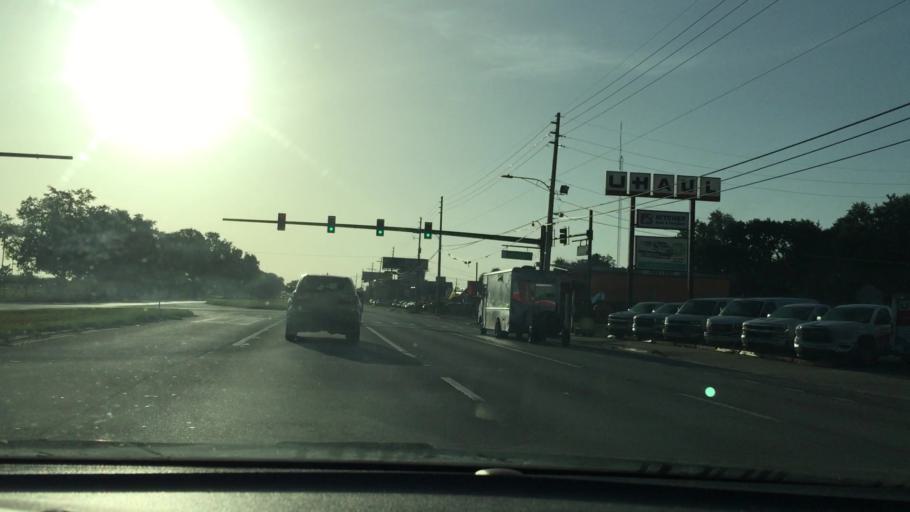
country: US
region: Florida
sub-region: Orange County
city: Pine Hills
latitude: 28.5534
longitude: -81.4400
